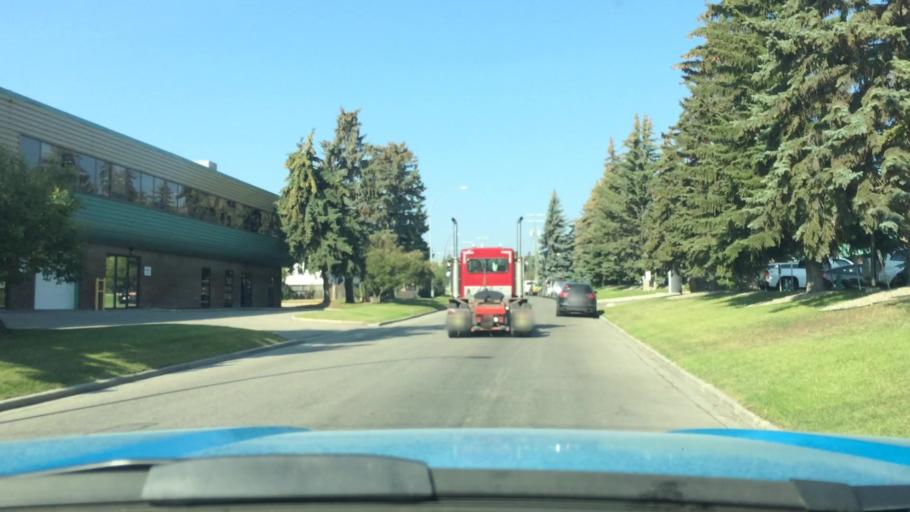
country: CA
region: Alberta
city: Calgary
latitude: 50.9889
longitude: -114.0487
